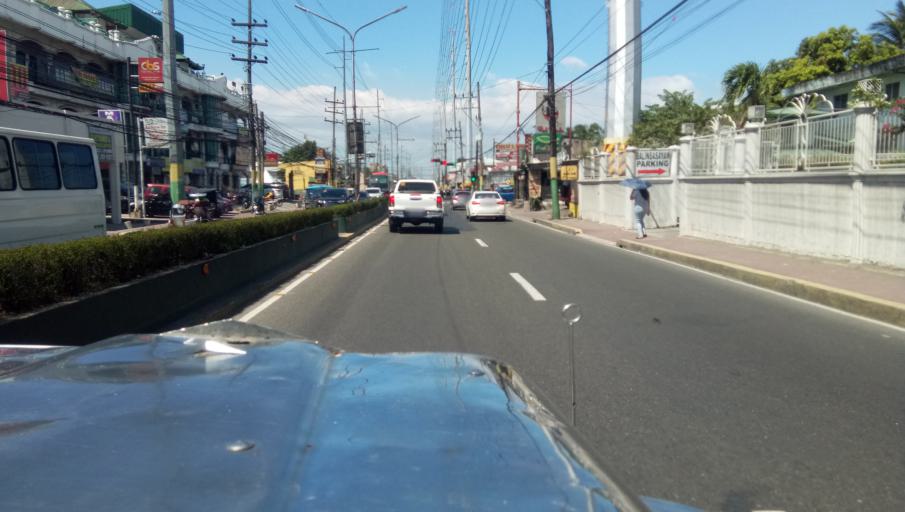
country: PH
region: Calabarzon
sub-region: Province of Cavite
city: Dasmarinas
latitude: 14.3309
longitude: 120.9393
